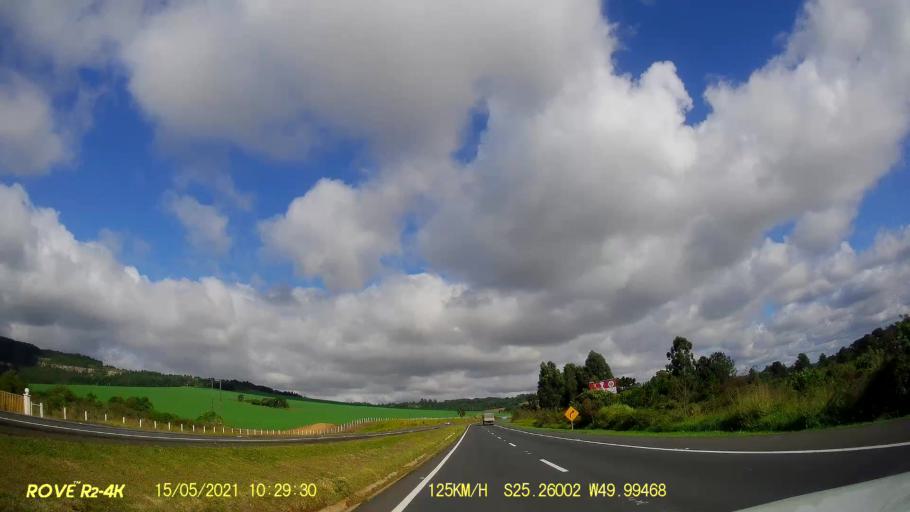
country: BR
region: Parana
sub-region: Palmeira
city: Palmeira
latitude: -25.2601
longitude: -49.9948
